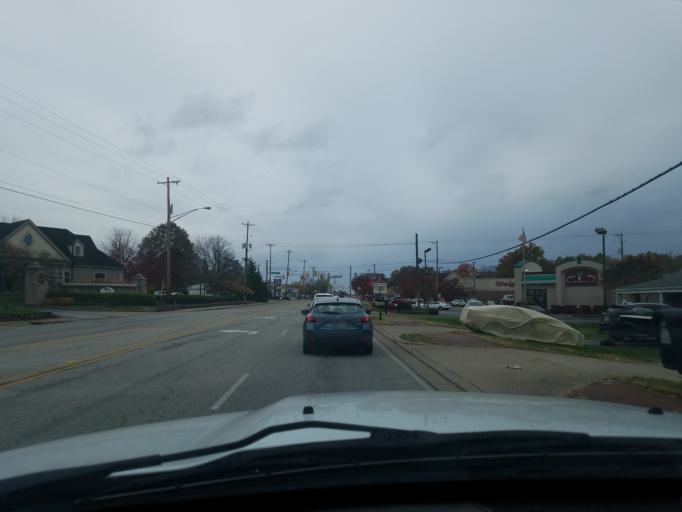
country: US
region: Indiana
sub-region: Floyd County
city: New Albany
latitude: 38.3259
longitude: -85.8008
